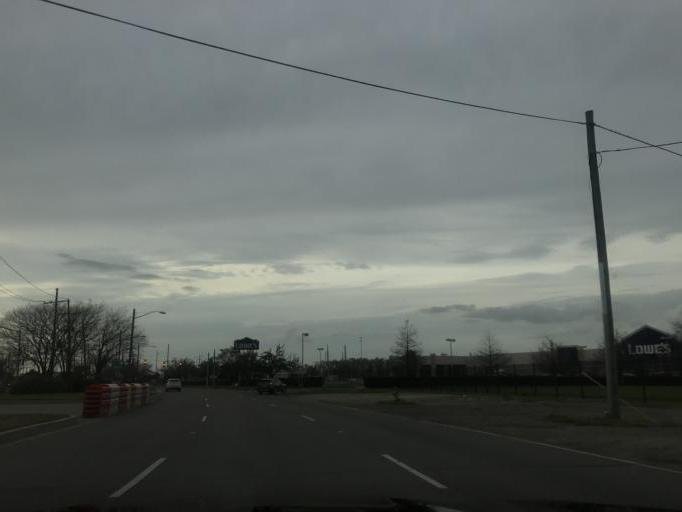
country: US
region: Louisiana
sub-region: Jefferson Parish
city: Jefferson
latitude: 29.9641
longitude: -90.1305
